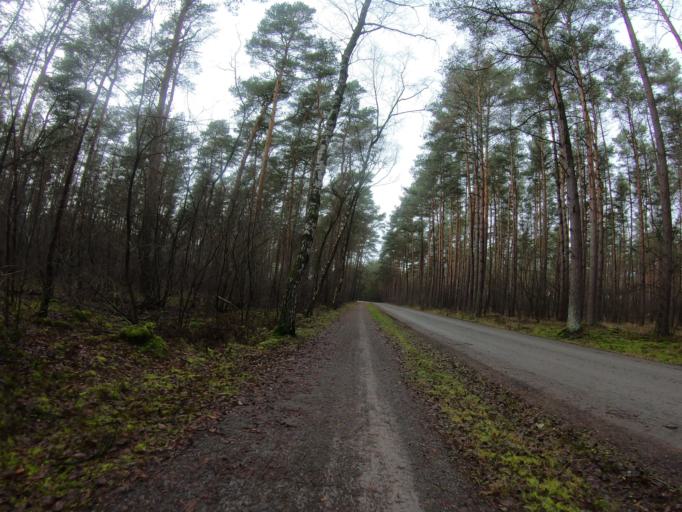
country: DE
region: Lower Saxony
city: Muden
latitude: 52.5094
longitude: 10.4249
